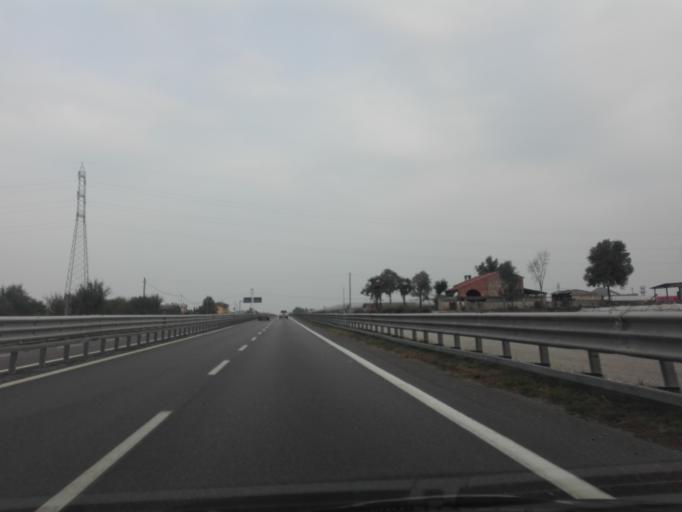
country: IT
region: Veneto
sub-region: Provincia di Verona
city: Vallese
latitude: 45.3367
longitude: 11.0746
